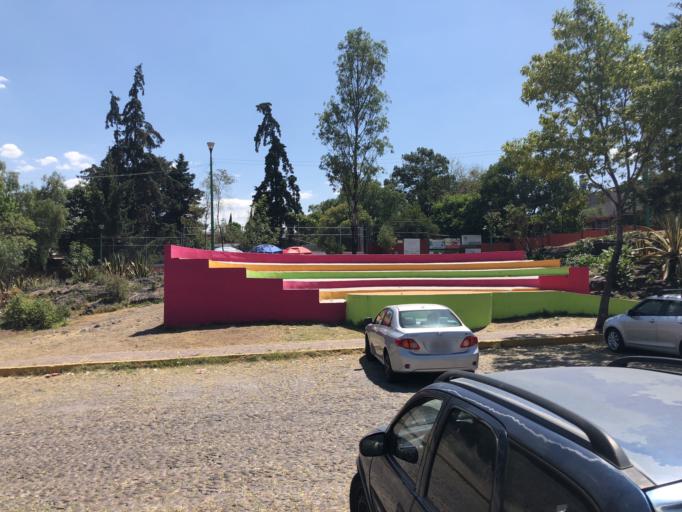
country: MX
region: Mexico City
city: Tlalpan
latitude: 19.3054
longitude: -99.1679
